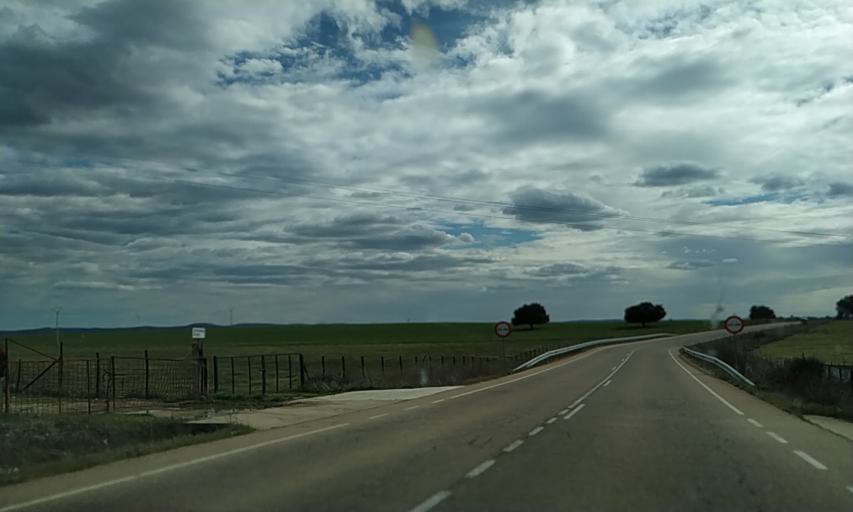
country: ES
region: Castille and Leon
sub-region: Provincia de Salamanca
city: Ciudad Rodrigo
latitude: 40.5666
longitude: -6.5480
